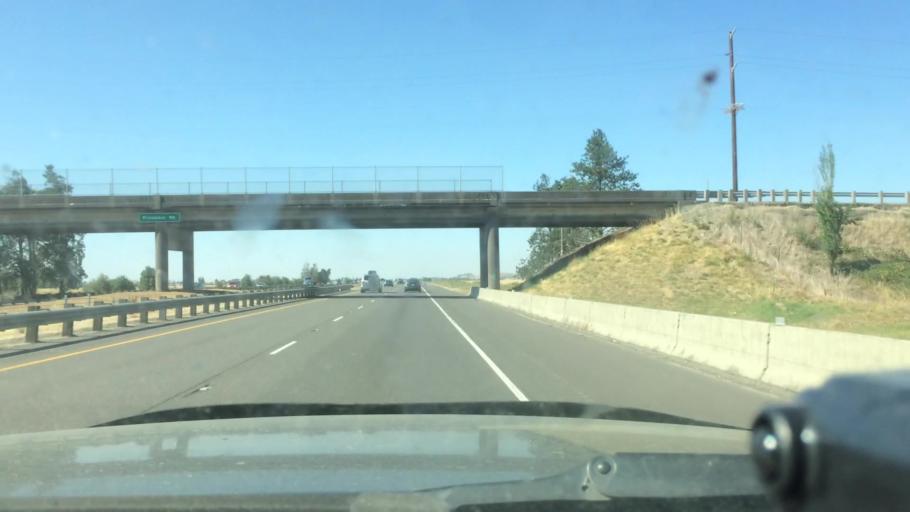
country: US
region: Oregon
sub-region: Linn County
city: Harrisburg
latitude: 44.2504
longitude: -123.0606
